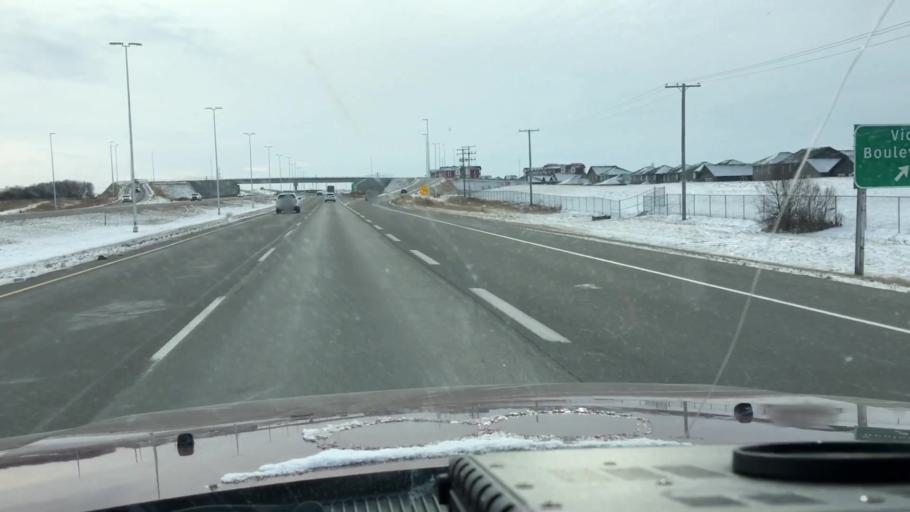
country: CA
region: Saskatchewan
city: Saskatoon
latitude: 52.0821
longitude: -106.6050
